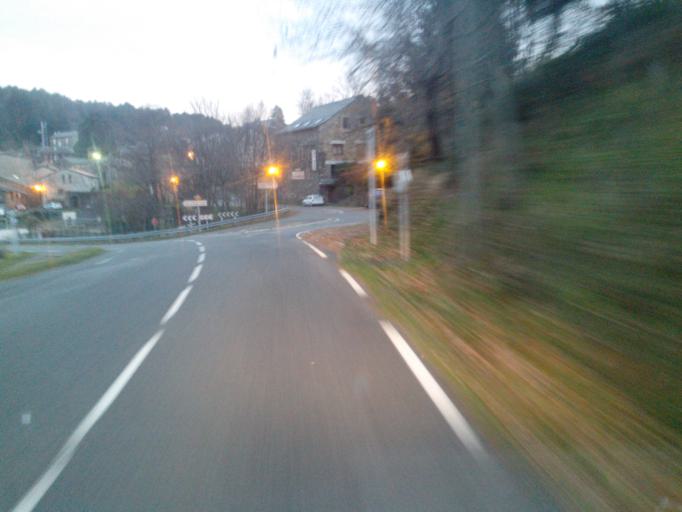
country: FR
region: Languedoc-Roussillon
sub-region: Departement du Gard
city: Saint-Jean-du-Gard
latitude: 44.1488
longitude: 3.7708
